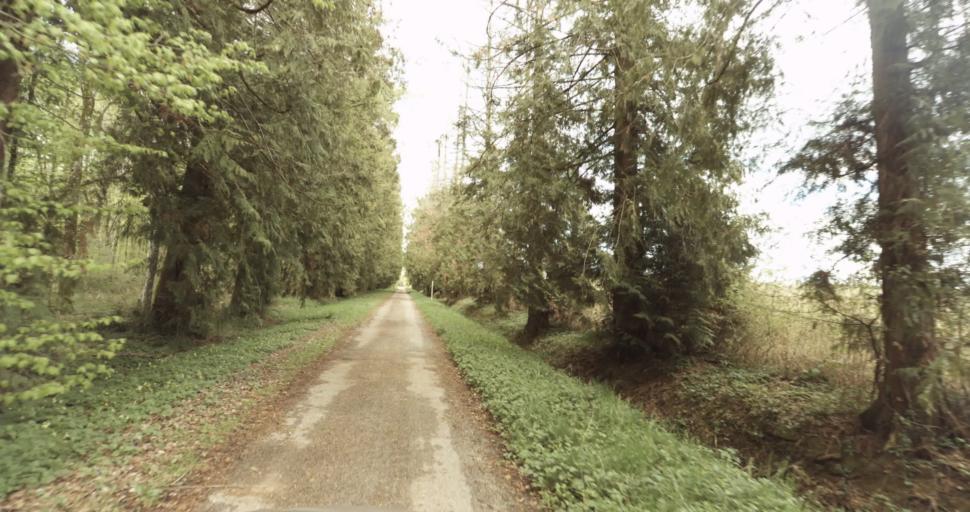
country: FR
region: Bourgogne
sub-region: Departement de la Cote-d'Or
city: Auxonne
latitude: 47.1618
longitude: 5.4230
